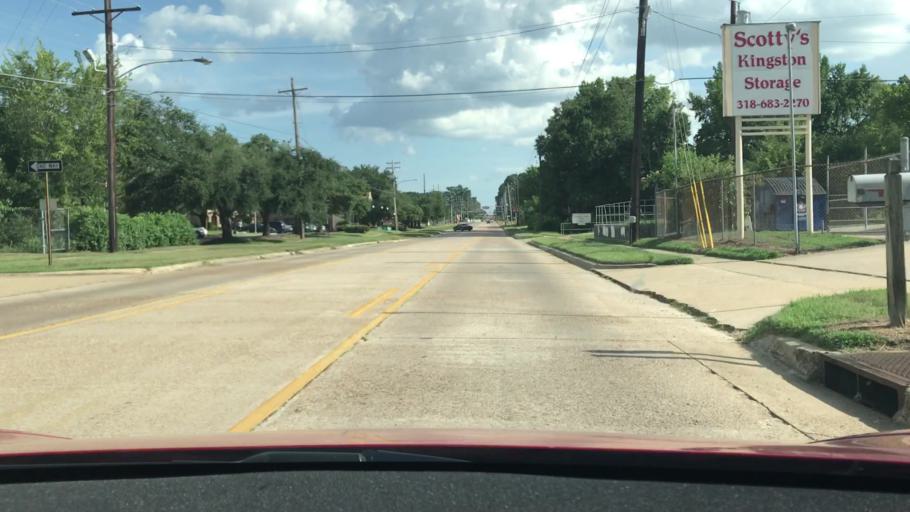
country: US
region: Louisiana
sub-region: Bossier Parish
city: Bossier City
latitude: 32.4059
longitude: -93.7805
